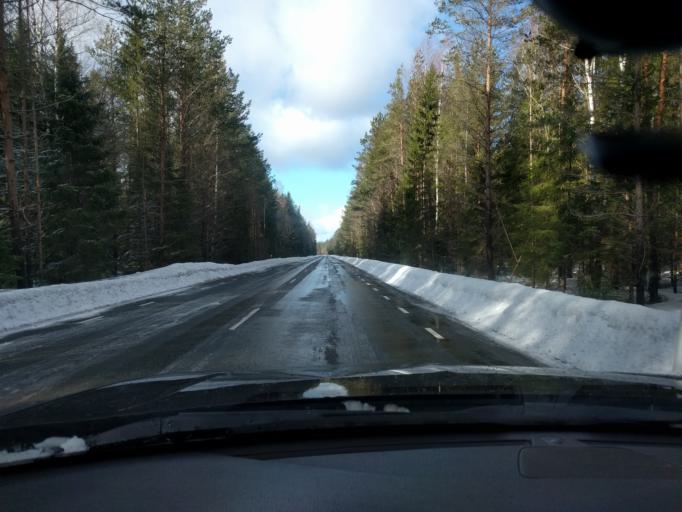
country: EE
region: Harju
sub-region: Kuusalu vald
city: Kuusalu
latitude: 59.2081
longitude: 25.5550
